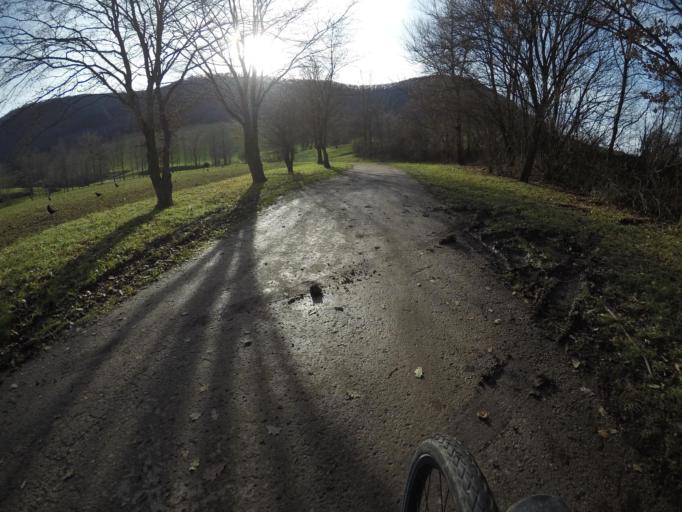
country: DE
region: Baden-Wuerttemberg
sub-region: Regierungsbezirk Stuttgart
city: Owen
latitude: 48.5792
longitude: 9.4320
